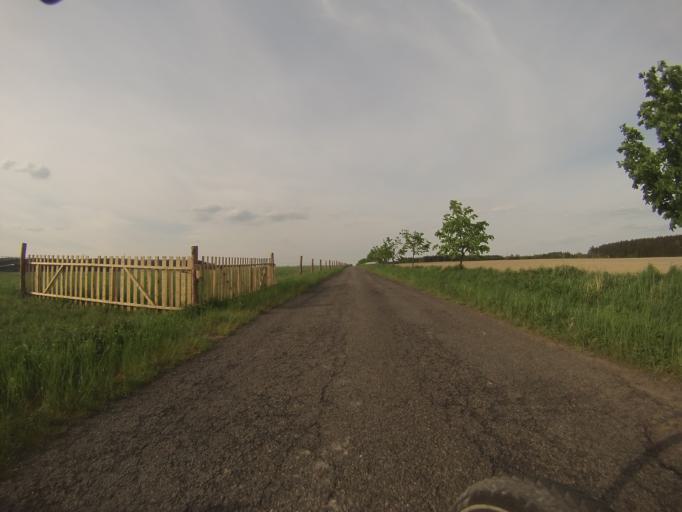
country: CZ
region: Olomoucky
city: Protivanov
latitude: 49.4495
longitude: 16.8643
